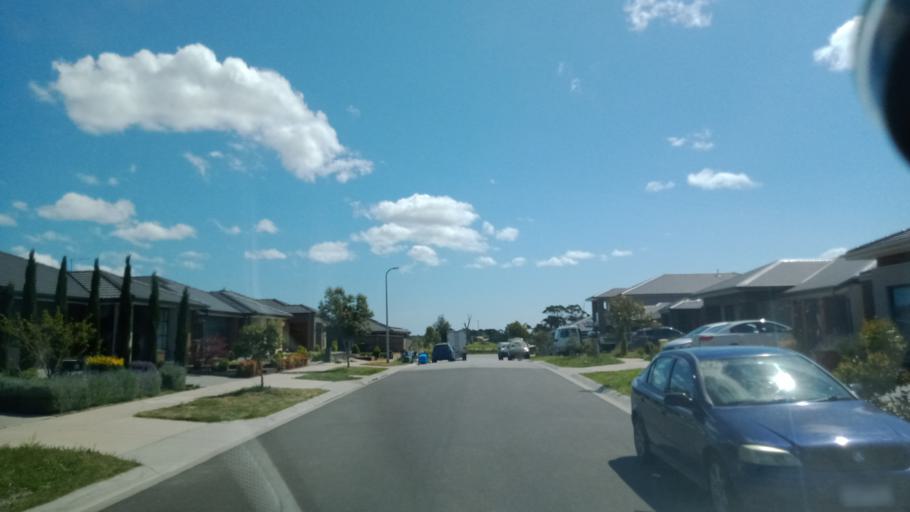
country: AU
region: Victoria
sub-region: Casey
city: Cranbourne West
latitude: -38.0988
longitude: 145.2463
